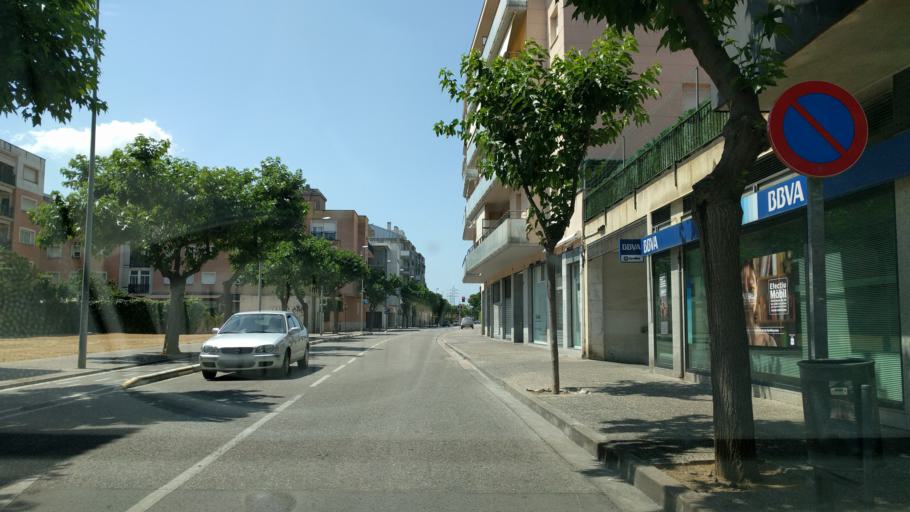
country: ES
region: Catalonia
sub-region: Provincia de Girona
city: Salt
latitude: 41.9739
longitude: 2.8052
